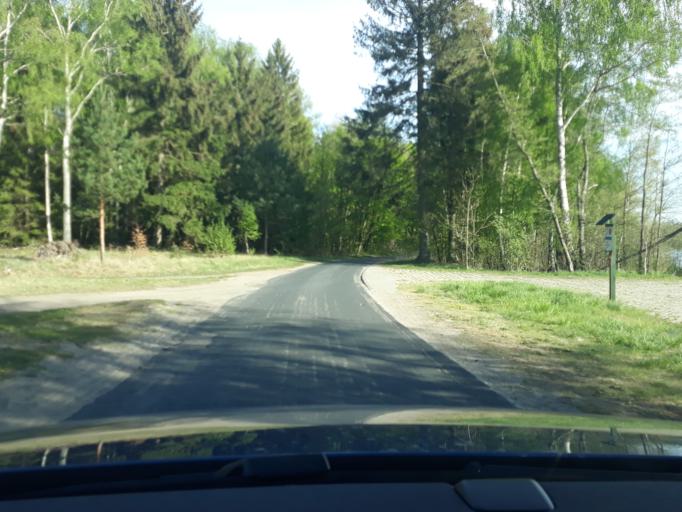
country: PL
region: Pomeranian Voivodeship
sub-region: Powiat czluchowski
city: Przechlewo
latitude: 53.8759
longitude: 17.3288
